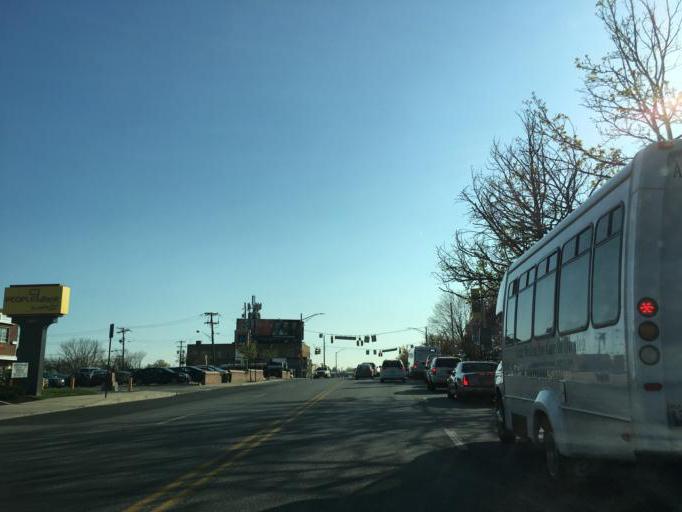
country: US
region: Maryland
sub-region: Baltimore County
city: Overlea
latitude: 39.3388
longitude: -76.5506
